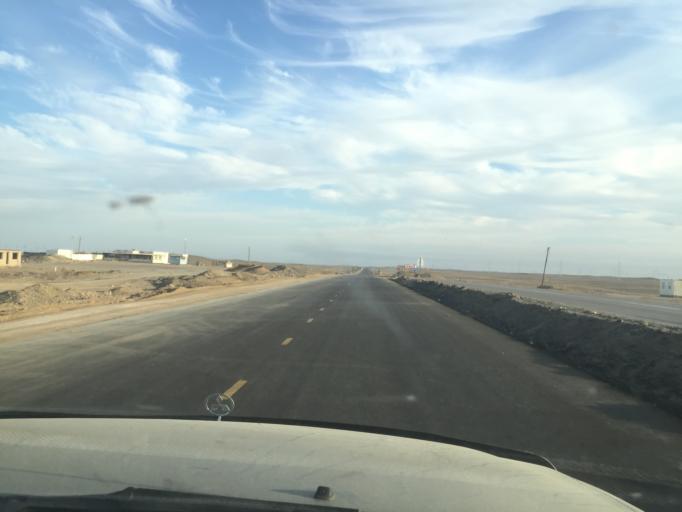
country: KZ
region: Almaty Oblysy
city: Ulken
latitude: 45.2347
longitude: 73.8367
